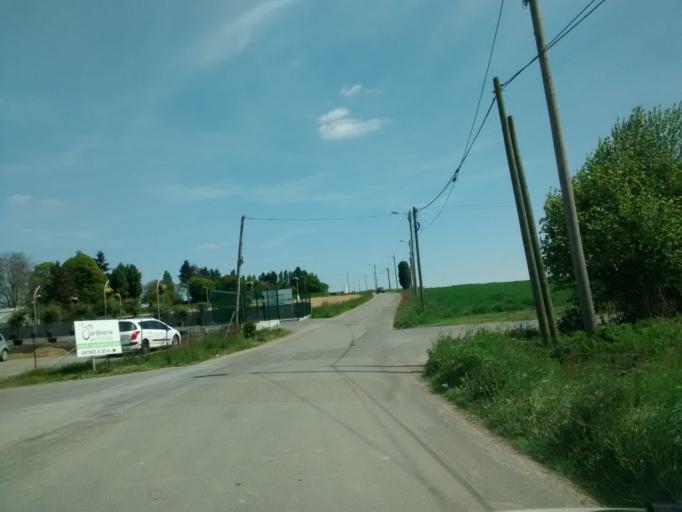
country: FR
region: Brittany
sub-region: Departement d'Ille-et-Vilaine
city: La Chapelle-des-Fougeretz
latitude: 48.1761
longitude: -1.7118
